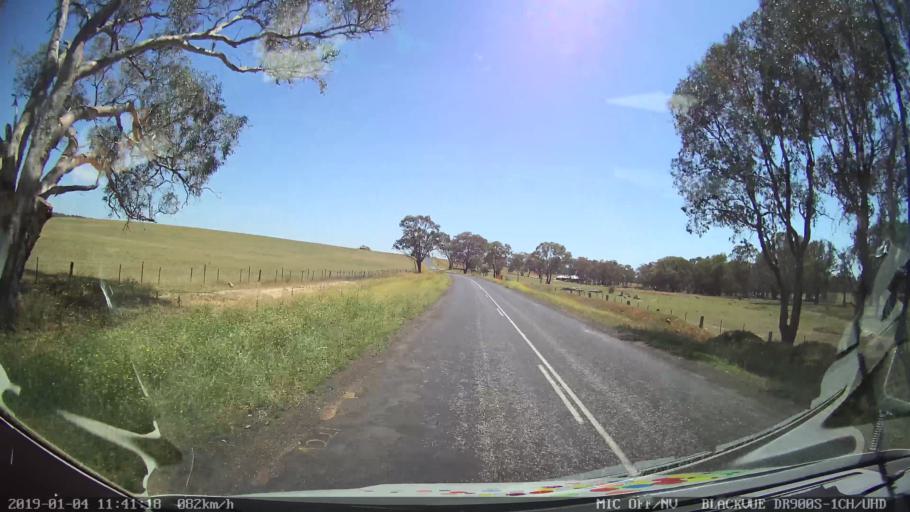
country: AU
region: New South Wales
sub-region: Cabonne
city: Molong
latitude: -32.9954
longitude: 148.7873
